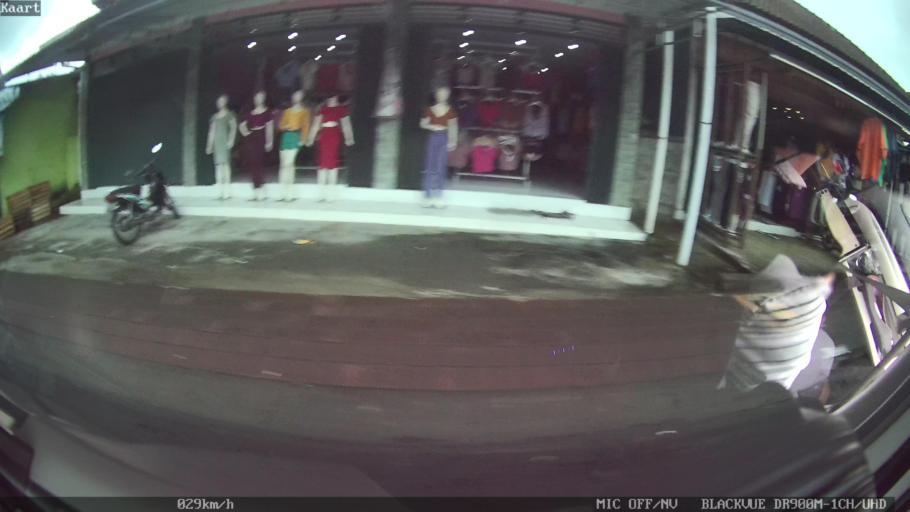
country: ID
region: Bali
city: Banjar Sempidi
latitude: -8.5213
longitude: 115.2095
